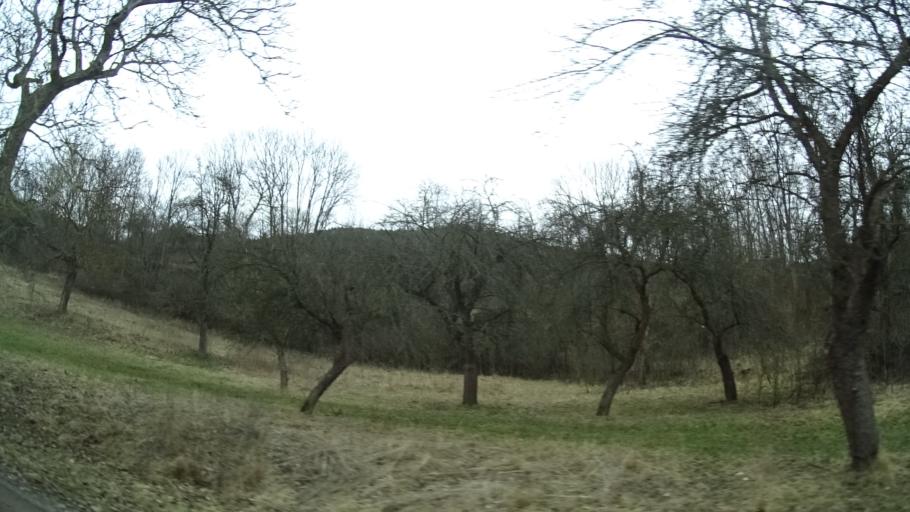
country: DE
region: Thuringia
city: Bad Blankenburg
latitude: 50.6975
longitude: 11.2515
